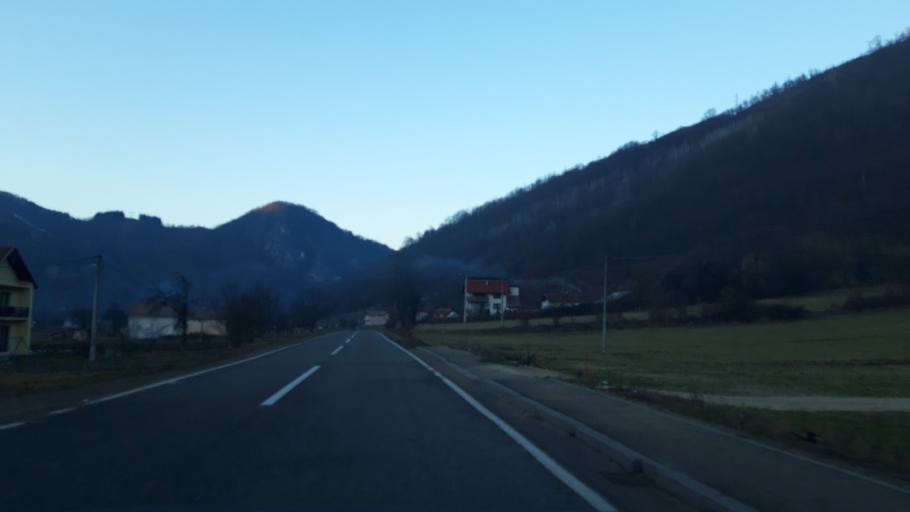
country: BA
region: Republika Srpska
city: Milici
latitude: 44.2559
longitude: 19.1079
